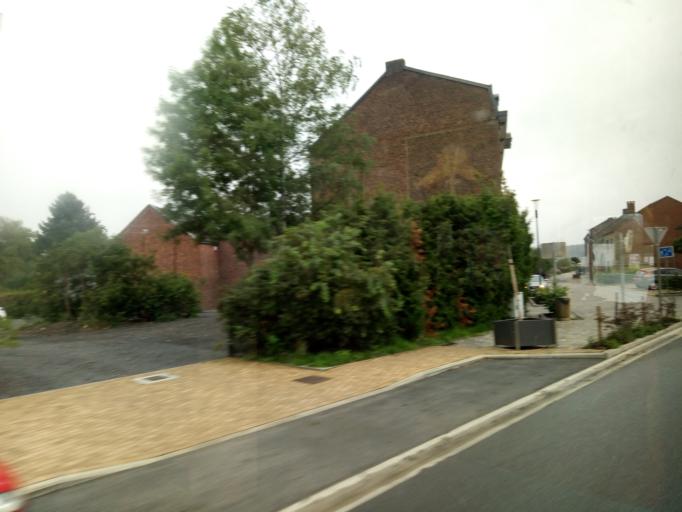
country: BE
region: Wallonia
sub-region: Province du Luxembourg
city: Hotton
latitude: 50.2788
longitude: 5.4402
